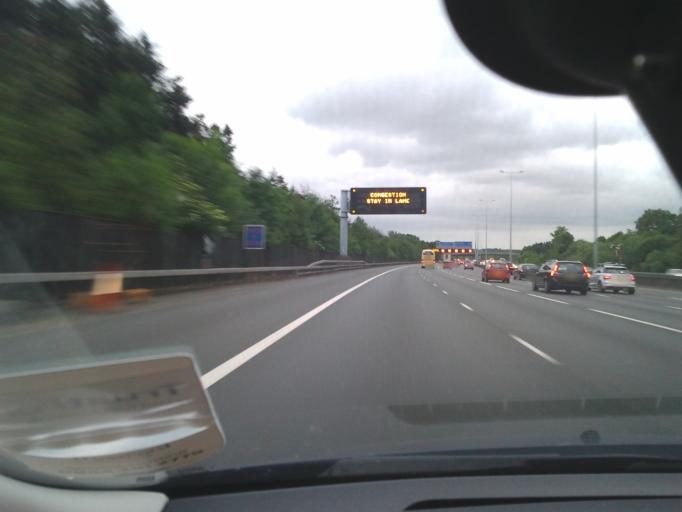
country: GB
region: England
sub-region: Surrey
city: Egham
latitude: 51.4187
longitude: -0.5394
